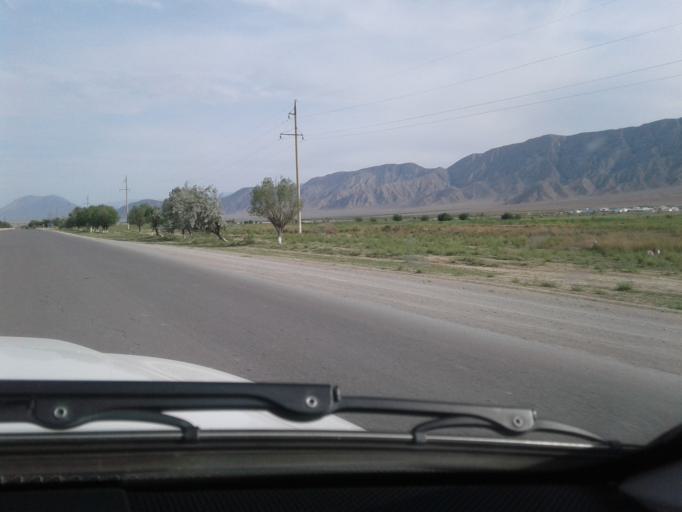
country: TM
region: Ahal
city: Arcabil
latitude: 38.1954
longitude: 57.8343
